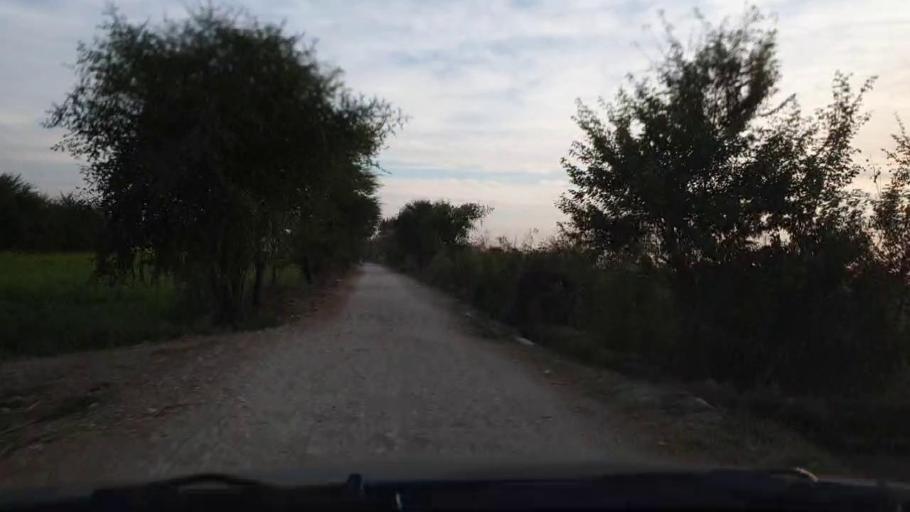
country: PK
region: Sindh
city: Khadro
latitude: 26.1223
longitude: 68.7781
